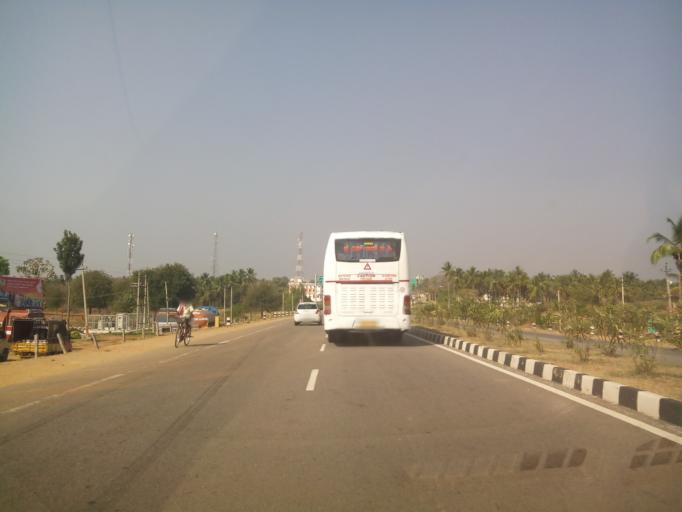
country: IN
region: Karnataka
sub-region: Mandya
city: Belluru
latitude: 12.9848
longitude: 76.8685
